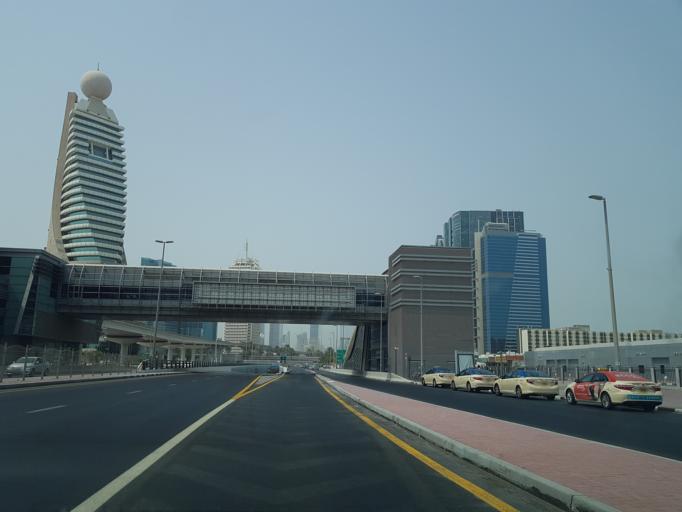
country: AE
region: Ash Shariqah
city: Sharjah
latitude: 25.2339
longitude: 55.2919
